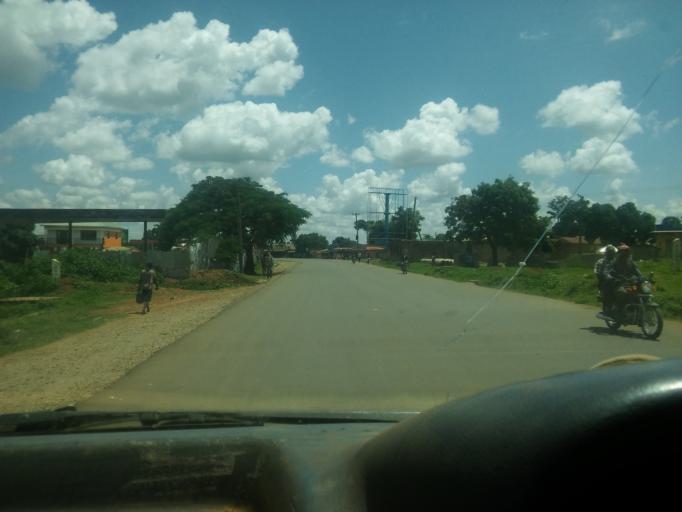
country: UG
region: Eastern Region
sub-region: Mbale District
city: Mbale
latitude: 1.0790
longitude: 34.1557
